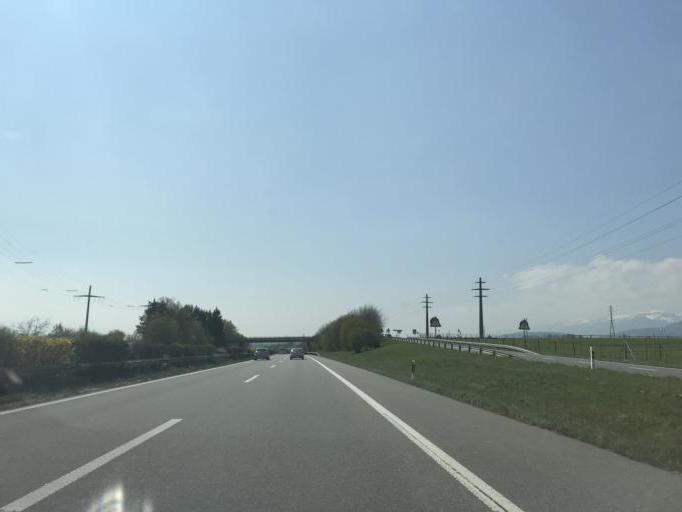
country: CH
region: Vaud
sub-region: Nyon District
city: Trelex
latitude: 46.3973
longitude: 6.2112
